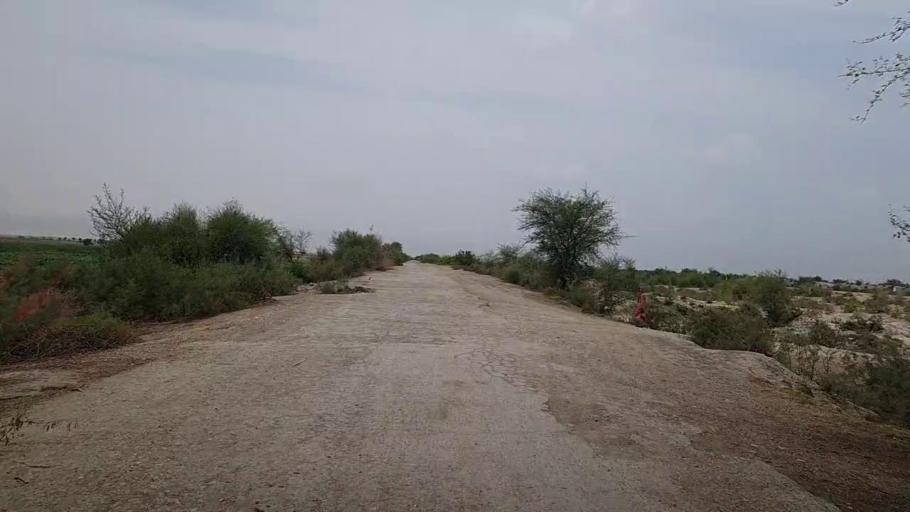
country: PK
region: Sindh
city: Sann
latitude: 26.2065
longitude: 67.9668
